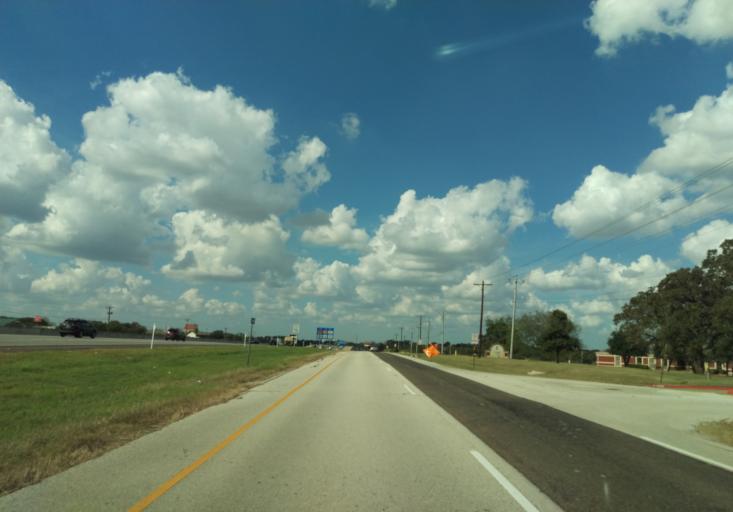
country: US
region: Texas
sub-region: Brazos County
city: College Station
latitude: 30.5678
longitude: -96.2684
